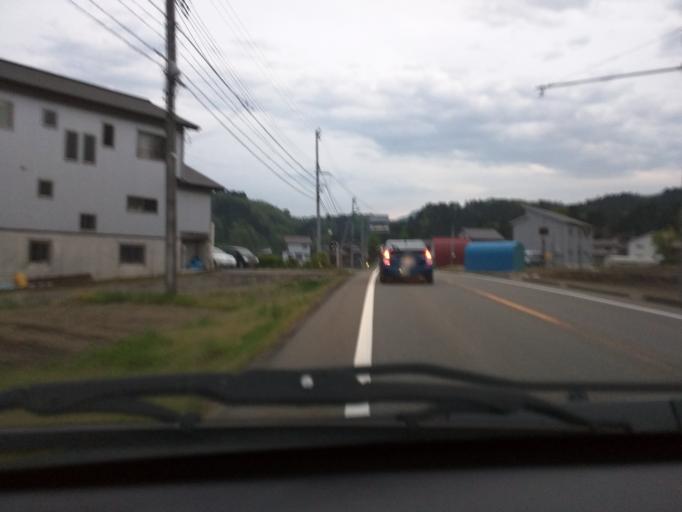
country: JP
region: Niigata
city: Ojiya
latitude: 37.3219
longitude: 138.7088
